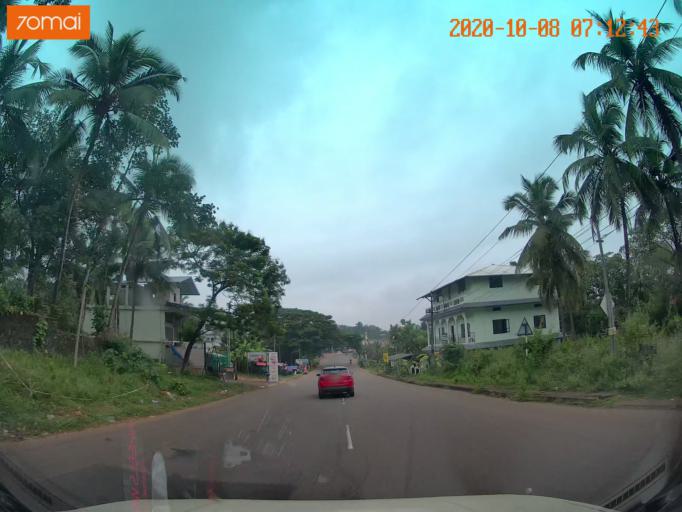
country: IN
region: Kerala
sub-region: Malappuram
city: Ponnani
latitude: 10.8061
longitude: 76.0078
